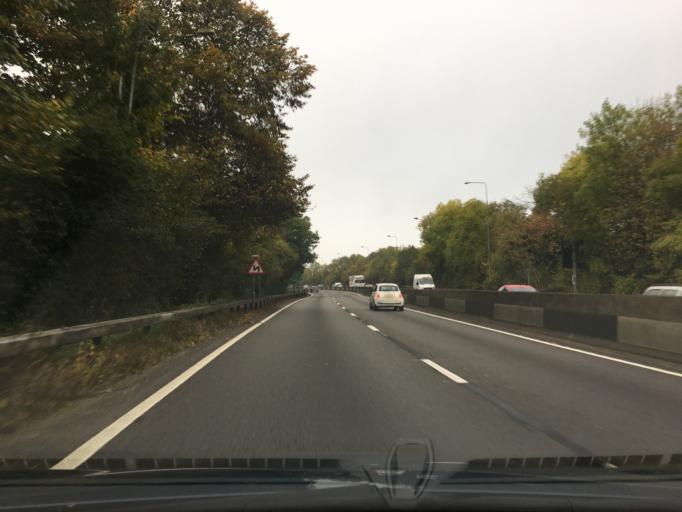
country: GB
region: England
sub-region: Surrey
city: Guildford
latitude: 51.2307
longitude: -0.6126
